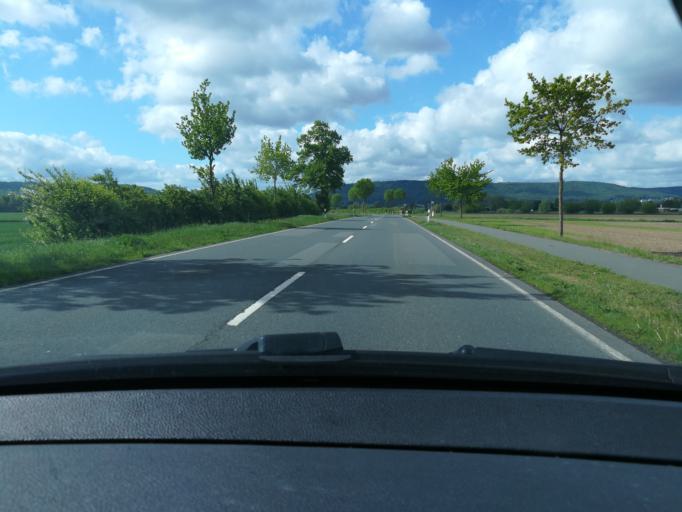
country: DE
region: North Rhine-Westphalia
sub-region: Regierungsbezirk Detmold
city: Minden
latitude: 52.2801
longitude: 8.9283
